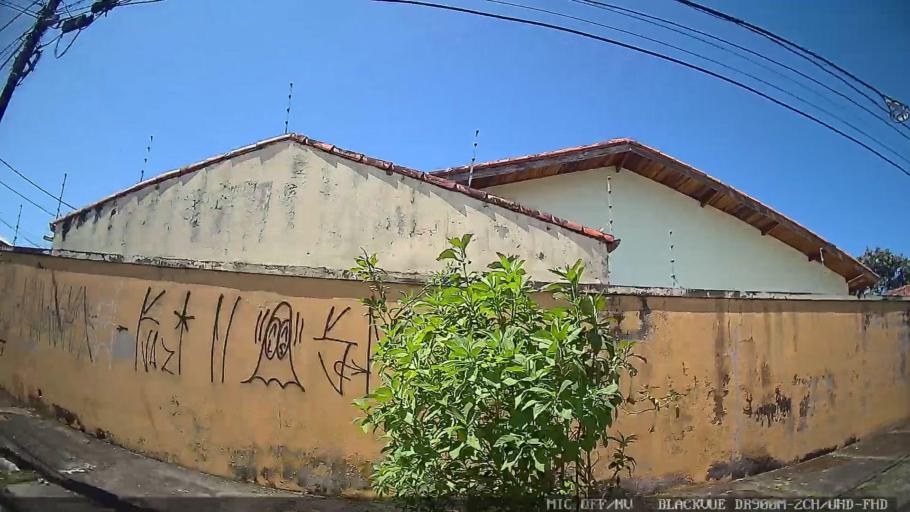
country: BR
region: Sao Paulo
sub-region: Peruibe
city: Peruibe
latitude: -24.3328
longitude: -47.0043
